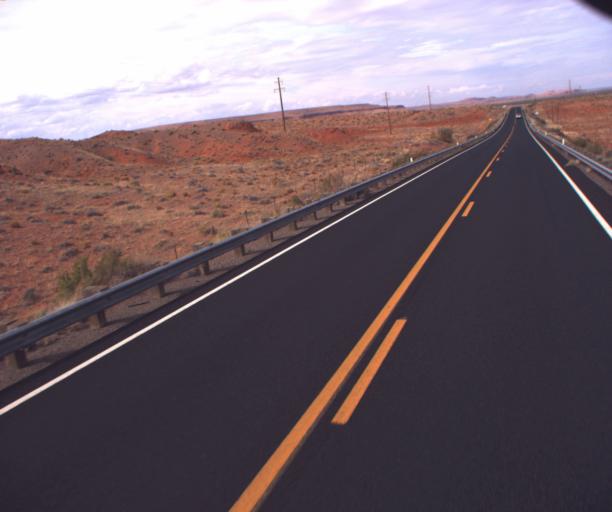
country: US
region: Arizona
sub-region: Apache County
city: Many Farms
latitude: 36.6013
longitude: -109.5699
